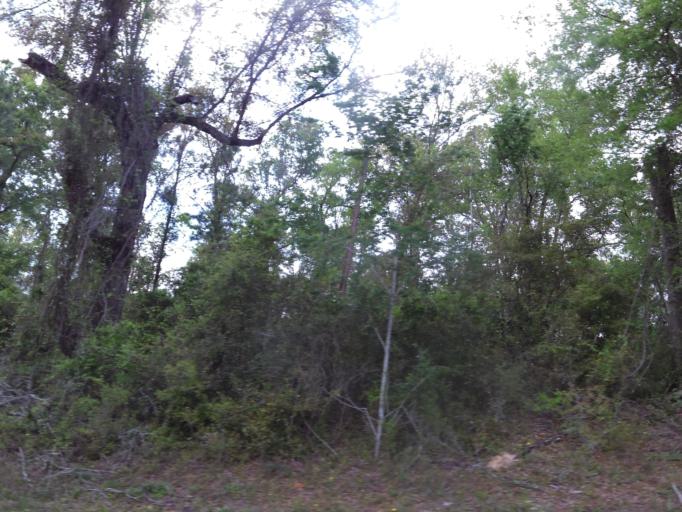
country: US
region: Georgia
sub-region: Charlton County
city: Folkston
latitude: 30.8282
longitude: -82.0329
